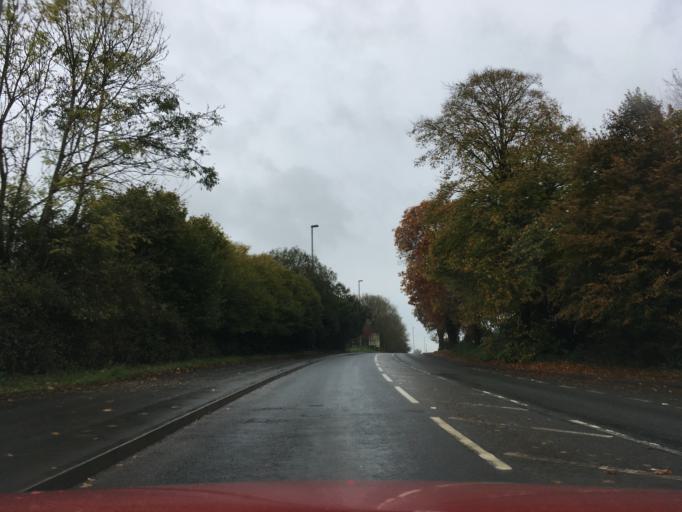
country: GB
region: Wales
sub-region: Newport
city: Langstone
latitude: 51.6069
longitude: -2.9006
